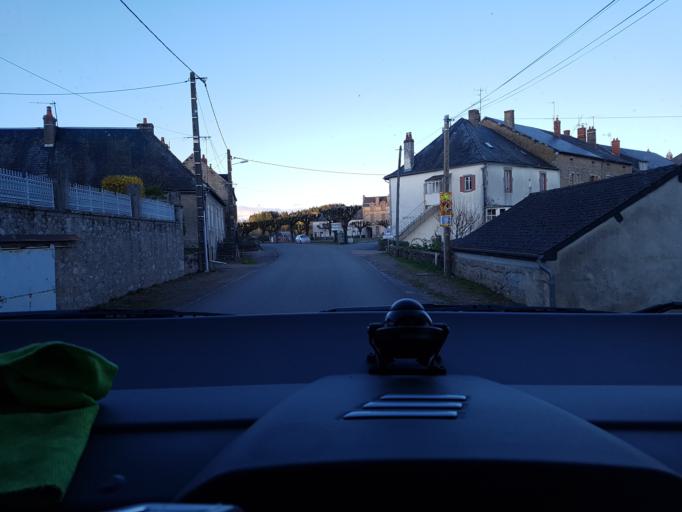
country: FR
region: Bourgogne
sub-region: Departement de Saone-et-Loire
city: Etang-sur-Arroux
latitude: 46.9223
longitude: 4.0994
